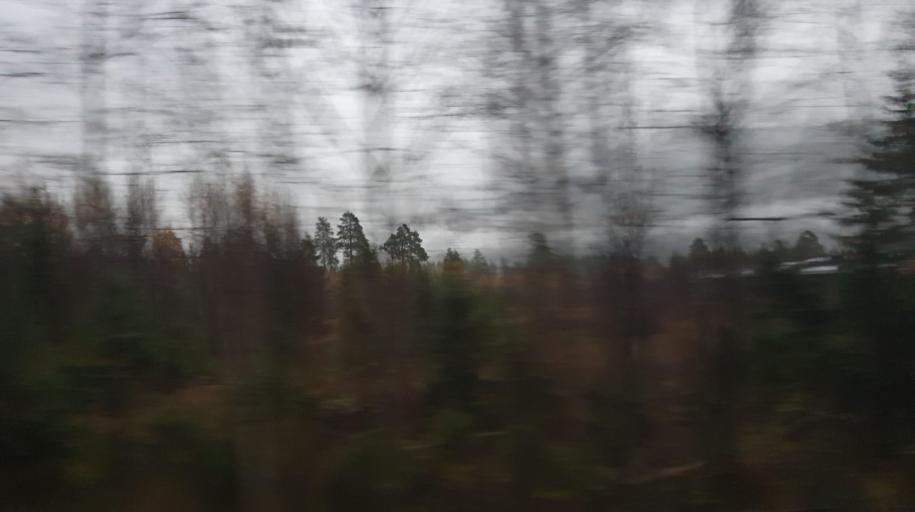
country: NO
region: Buskerud
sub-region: Krodsherad
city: Noresund
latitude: 60.1879
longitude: 9.5958
